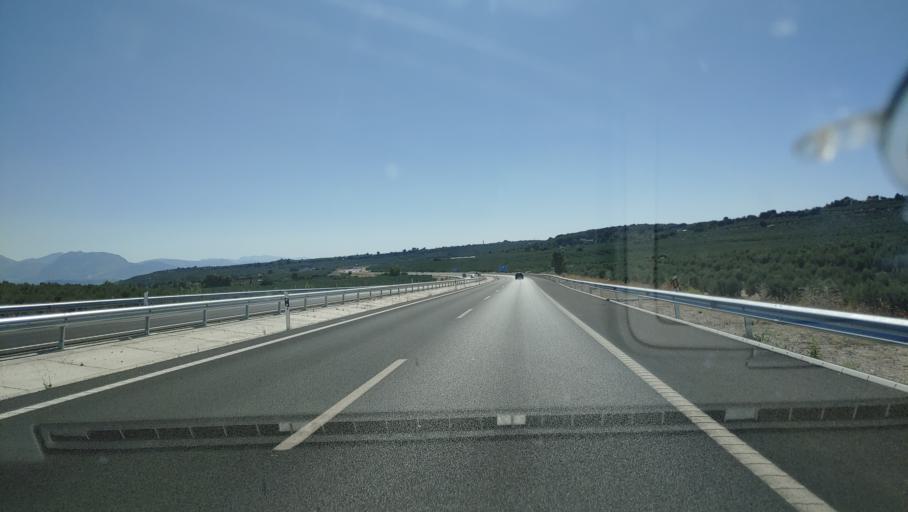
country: ES
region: Andalusia
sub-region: Provincia de Jaen
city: Sabiote
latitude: 38.0435
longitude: -3.3150
